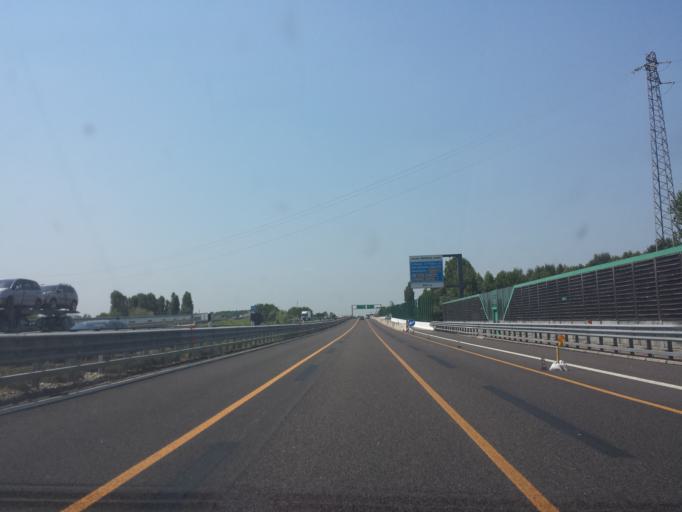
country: IT
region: Veneto
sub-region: Provincia di Padova
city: Vigodarzere
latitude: 45.4429
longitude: 11.8773
